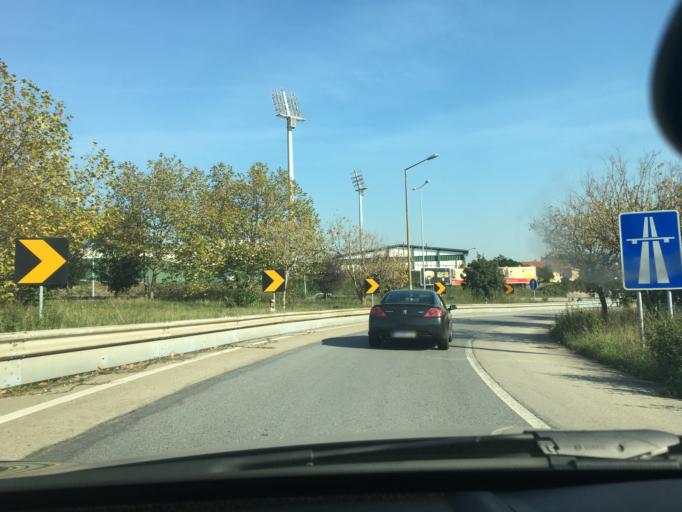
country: PT
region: Porto
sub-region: Matosinhos
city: Leca da Palmeira
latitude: 41.2025
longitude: -8.6907
